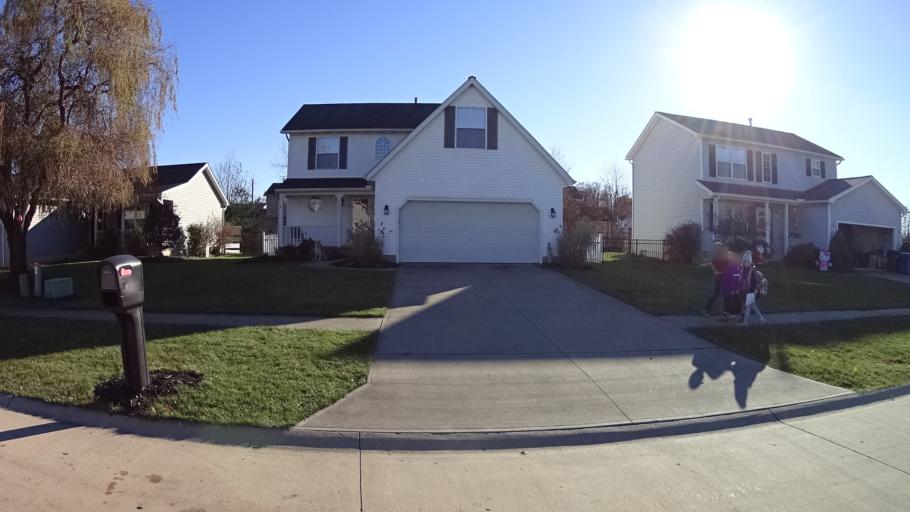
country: US
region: Ohio
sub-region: Lorain County
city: North Ridgeville
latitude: 41.4085
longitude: -82.0103
